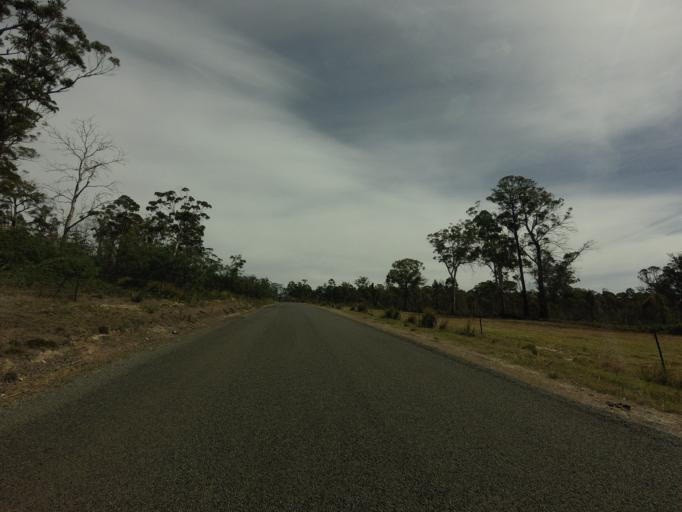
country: AU
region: Tasmania
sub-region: Sorell
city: Sorell
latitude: -42.5534
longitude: 147.6752
